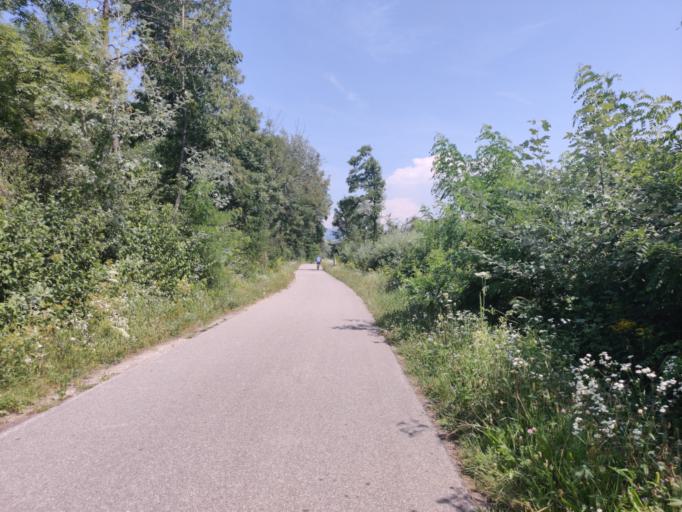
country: AT
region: Upper Austria
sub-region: Politischer Bezirk Urfahr-Umgebung
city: Ottensheim
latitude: 48.3202
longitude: 14.1430
